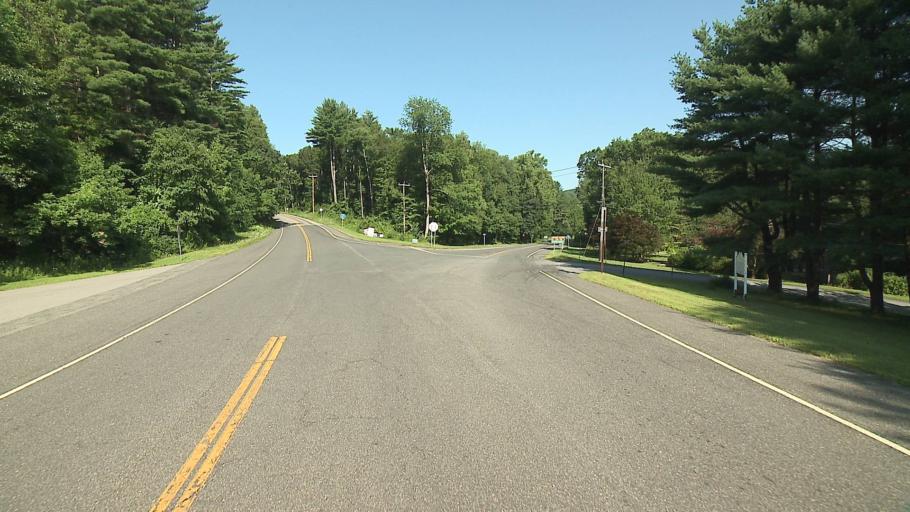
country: US
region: Connecticut
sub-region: Litchfield County
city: Kent
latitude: 41.8207
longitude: -73.3748
